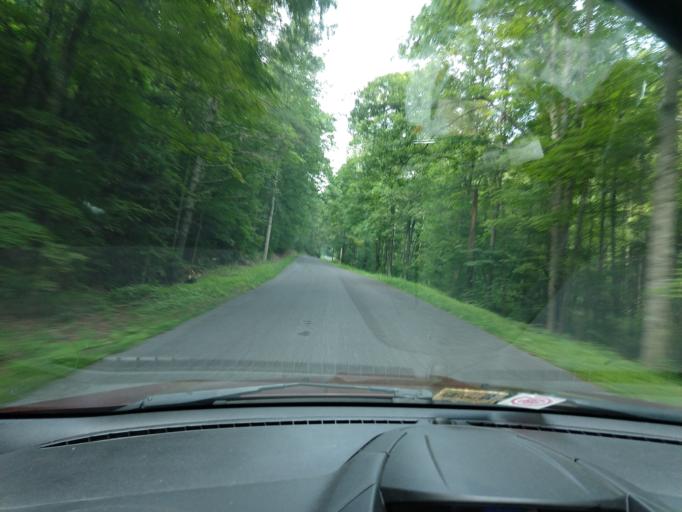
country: US
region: Virginia
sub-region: City of Covington
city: Covington
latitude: 37.9111
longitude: -80.0766
